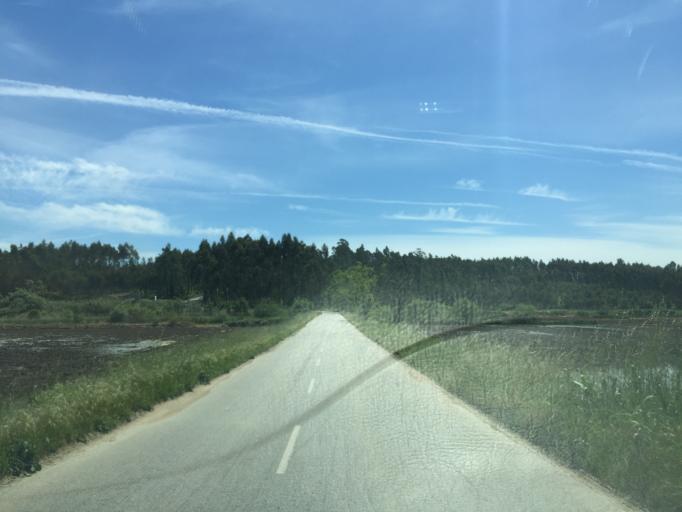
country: PT
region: Leiria
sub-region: Pombal
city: Lourical
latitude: 40.0675
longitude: -8.7584
